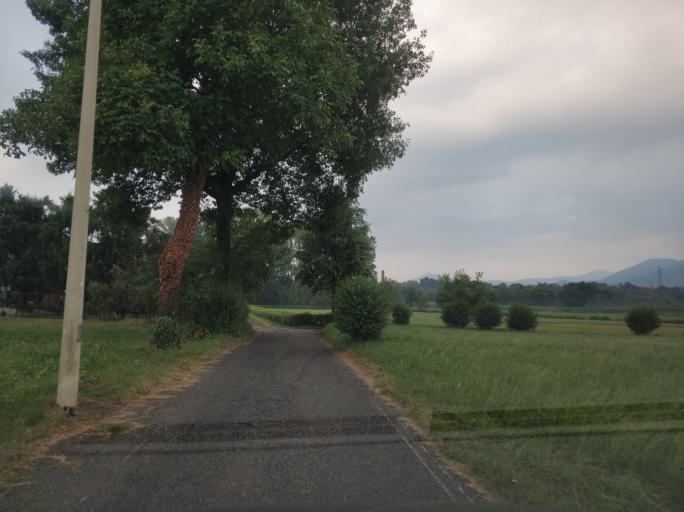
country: IT
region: Piedmont
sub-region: Provincia di Torino
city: Robassomero
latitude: 45.2062
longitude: 7.5833
